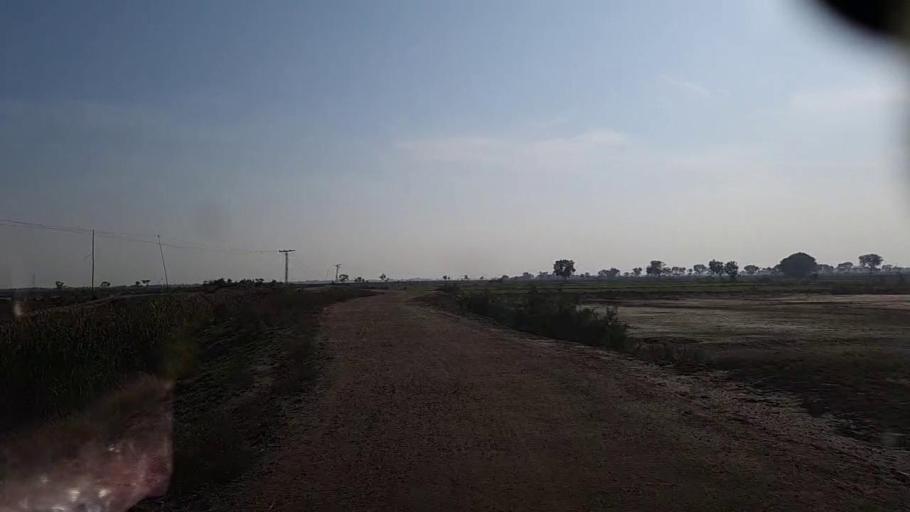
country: PK
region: Sindh
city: Jacobabad
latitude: 28.2978
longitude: 68.5578
